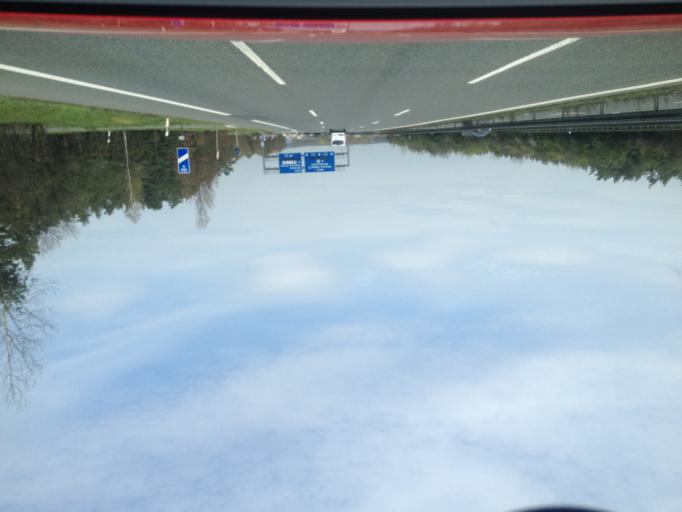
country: DE
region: Bavaria
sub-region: Regierungsbezirk Mittelfranken
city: Feucht
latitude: 49.3401
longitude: 11.2041
